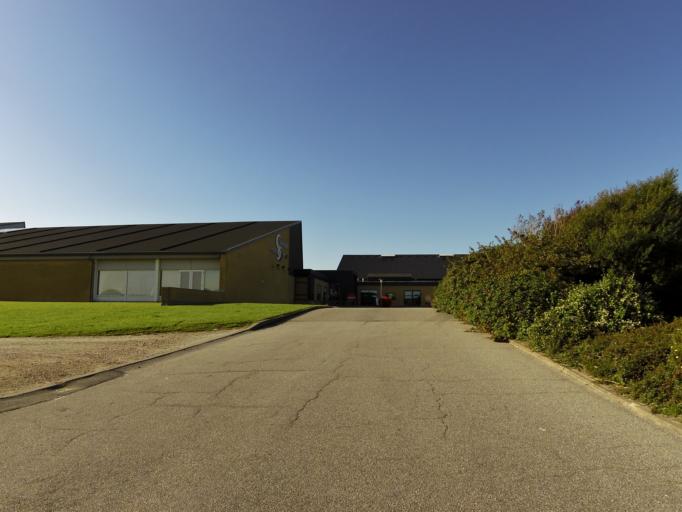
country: DK
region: South Denmark
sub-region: Tonder Kommune
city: Sherrebek
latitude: 55.1580
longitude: 8.7597
